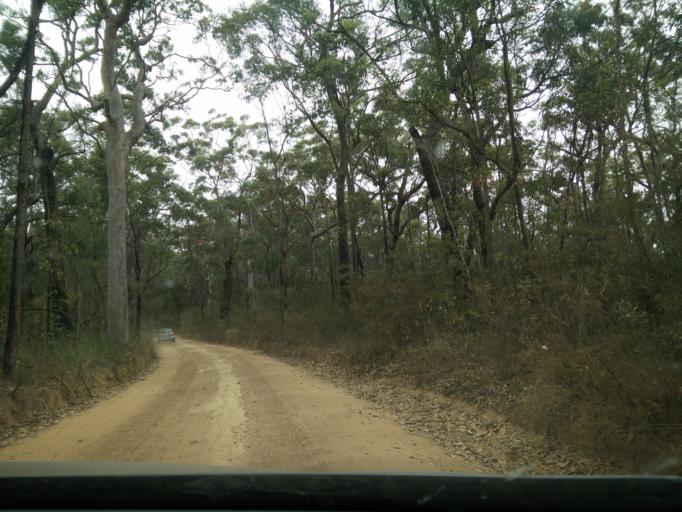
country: AU
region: New South Wales
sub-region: Blue Mountains Municipality
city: Glenbrook
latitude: -33.8118
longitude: 150.5682
